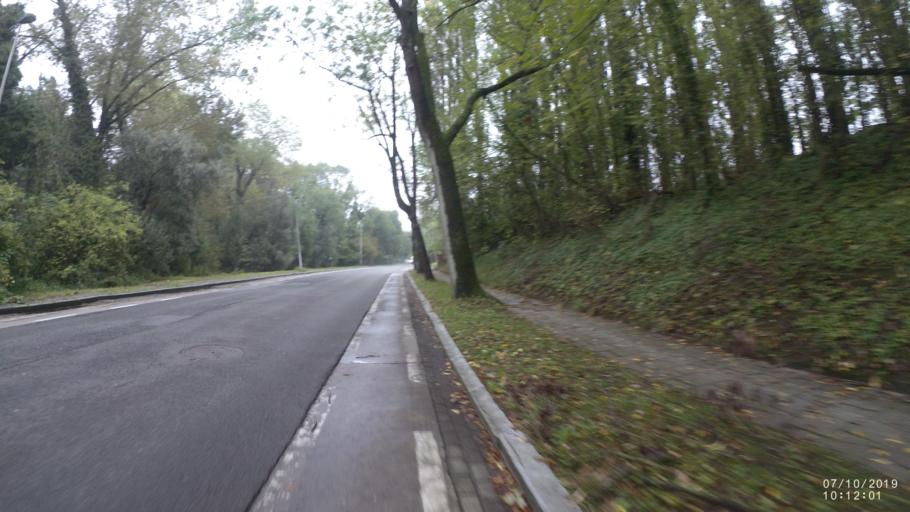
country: BE
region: Flanders
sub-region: Provincie Oost-Vlaanderen
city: Gent
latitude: 51.0409
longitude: 3.6953
